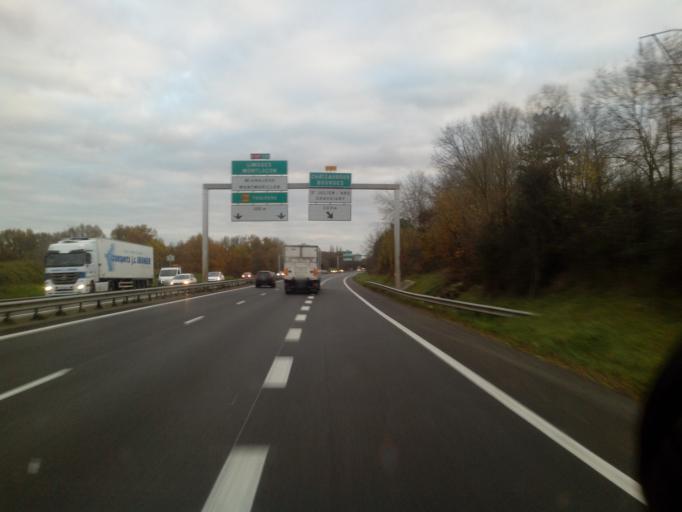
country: FR
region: Poitou-Charentes
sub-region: Departement de la Vienne
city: Mignaloux-Beauvoir
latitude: 46.5704
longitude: 0.3986
